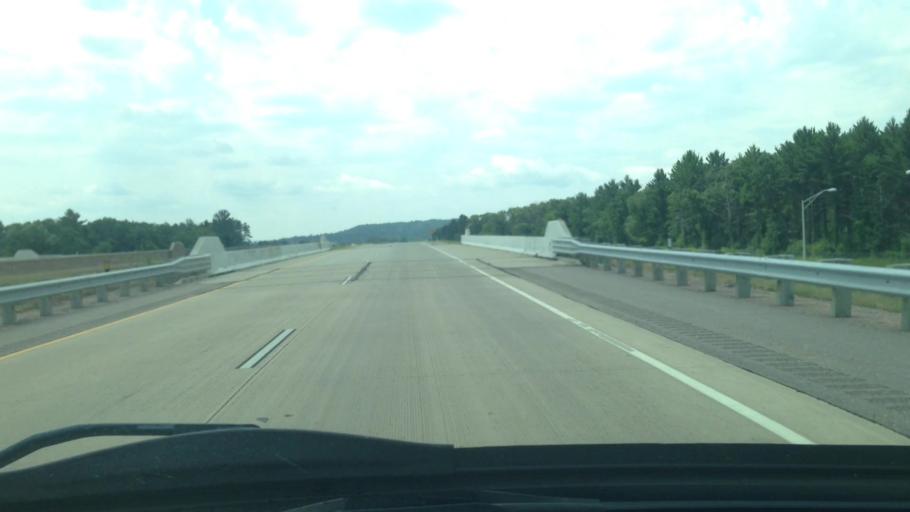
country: US
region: Wisconsin
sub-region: Sauk County
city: West Baraboo
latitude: 43.5331
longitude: -89.7871
